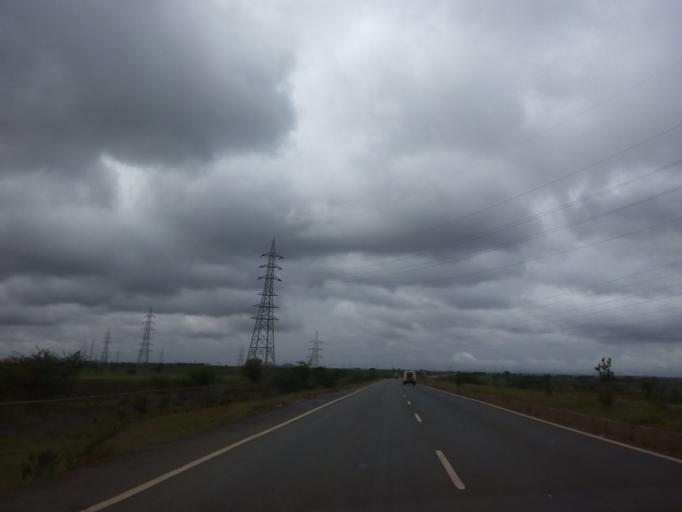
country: IN
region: Karnataka
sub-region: Haveri
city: Haveri
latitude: 14.8112
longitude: 75.3735
